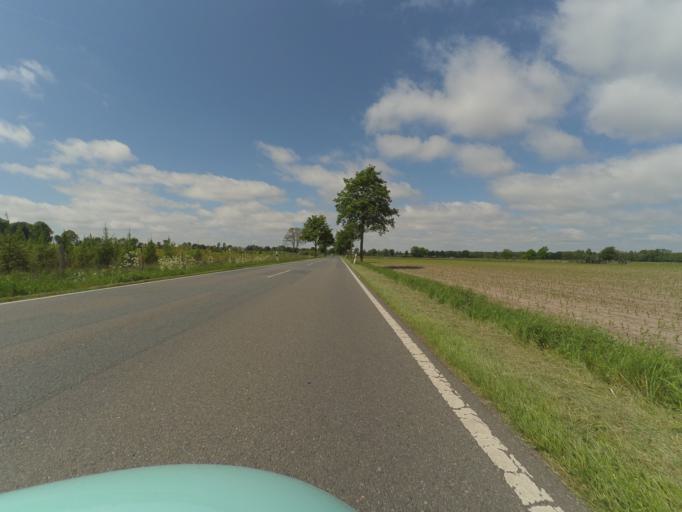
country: DE
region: Lower Saxony
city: Leiferde
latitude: 52.4381
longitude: 10.4566
